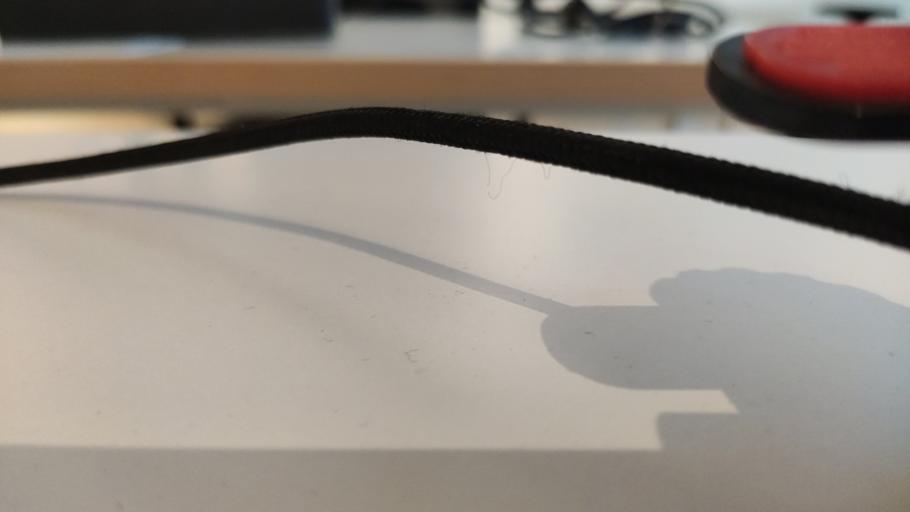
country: RU
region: Moskovskaya
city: Novopetrovskoye
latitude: 55.8760
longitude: 36.4071
